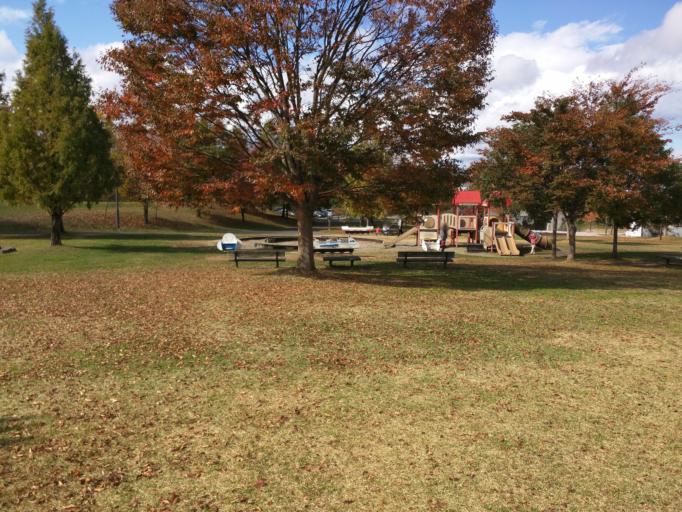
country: JP
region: Fukushima
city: Kitakata
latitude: 37.4601
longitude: 139.9297
